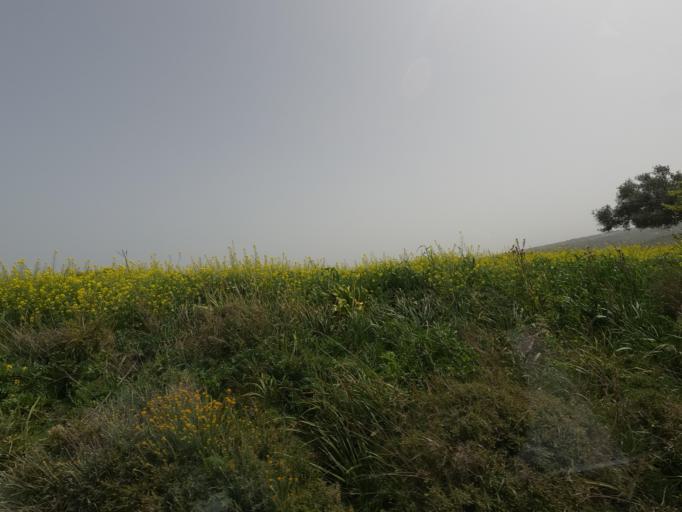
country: CY
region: Pafos
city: Polis
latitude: 34.9920
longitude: 32.3887
